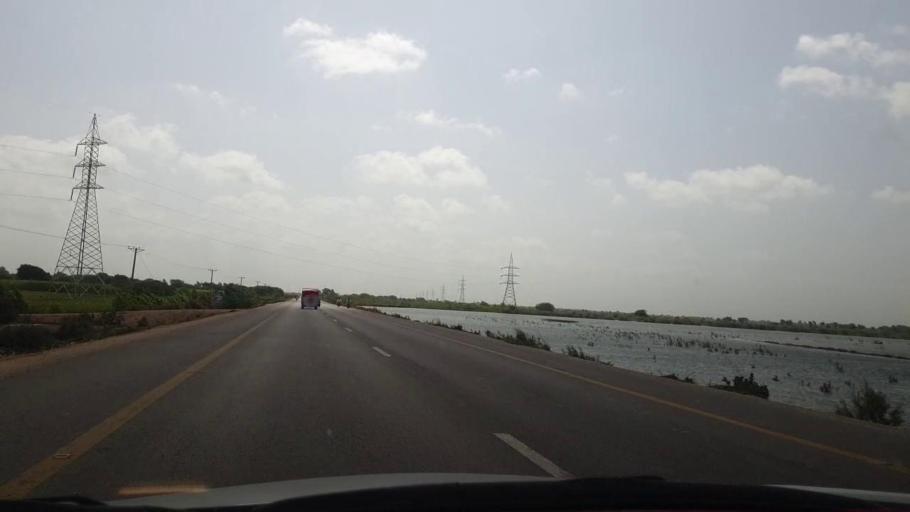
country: PK
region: Sindh
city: Talhar
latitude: 24.9253
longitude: 68.7186
